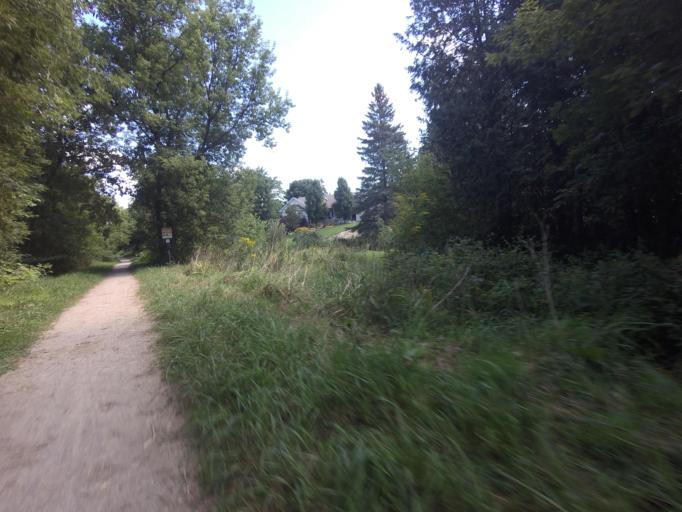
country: CA
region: Ontario
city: Orangeville
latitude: 43.7902
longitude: -80.3149
